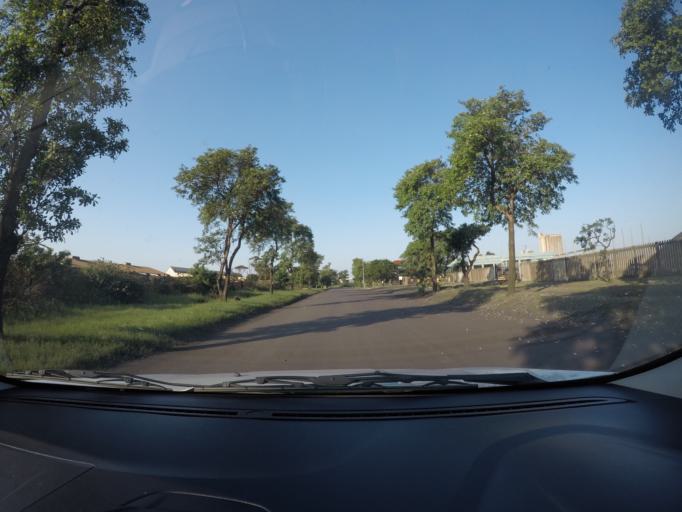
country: ZA
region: KwaZulu-Natal
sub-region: uThungulu District Municipality
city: Richards Bay
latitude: -28.7597
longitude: 32.0087
